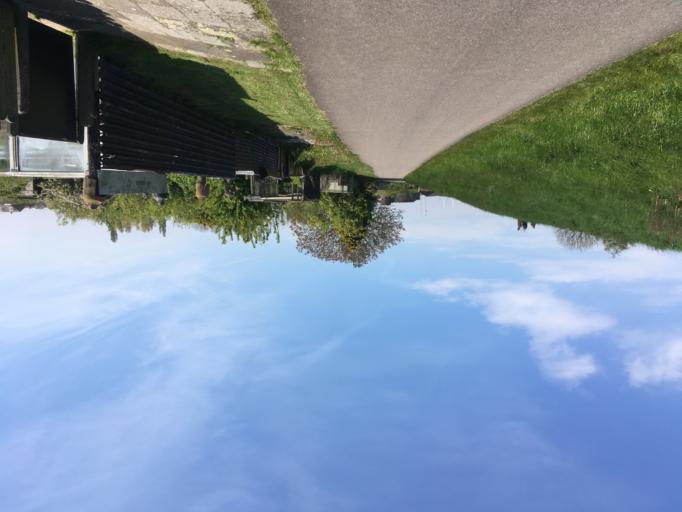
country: NL
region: North Holland
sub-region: Gemeente Weesp
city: Weesp
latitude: 52.3370
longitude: 5.0627
